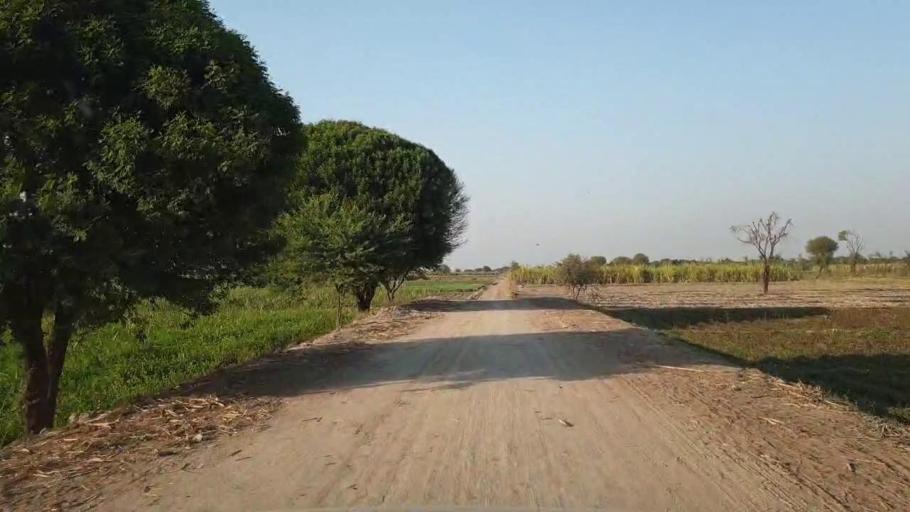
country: PK
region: Sindh
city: Tando Allahyar
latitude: 25.3411
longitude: 68.6934
